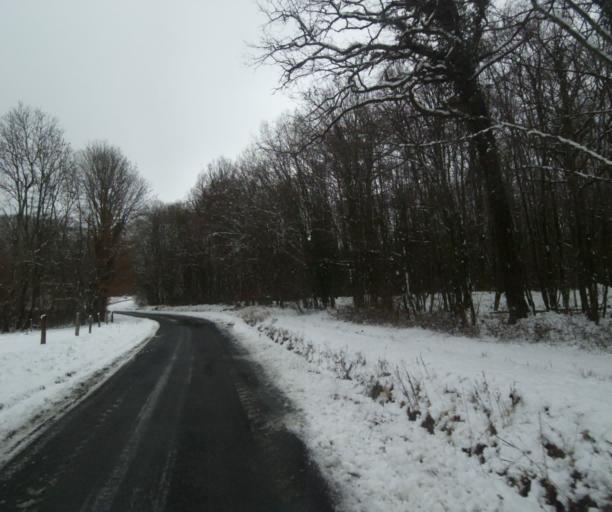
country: FR
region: Champagne-Ardenne
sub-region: Departement de la Haute-Marne
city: Laneuville-a-Remy
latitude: 48.4658
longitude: 4.9020
